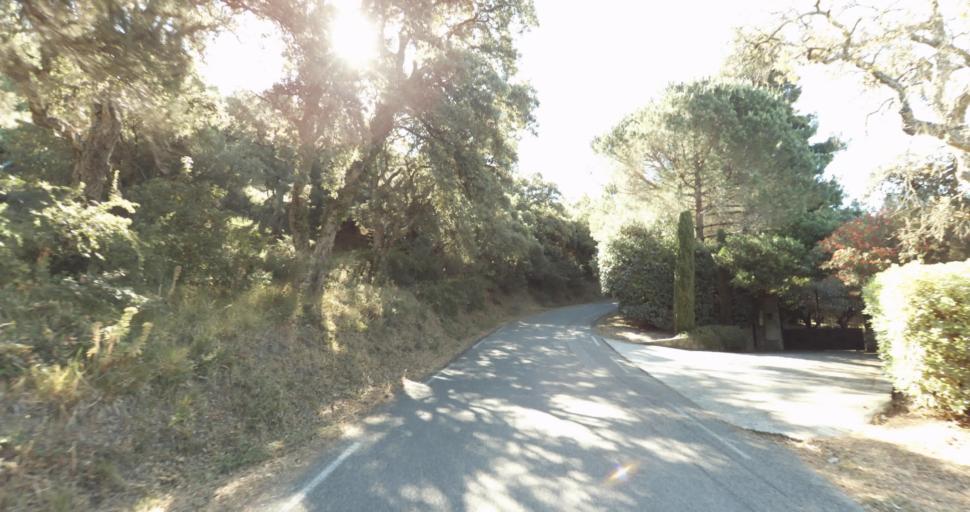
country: FR
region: Provence-Alpes-Cote d'Azur
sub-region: Departement du Var
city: Ramatuelle
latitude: 43.2183
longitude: 6.5969
